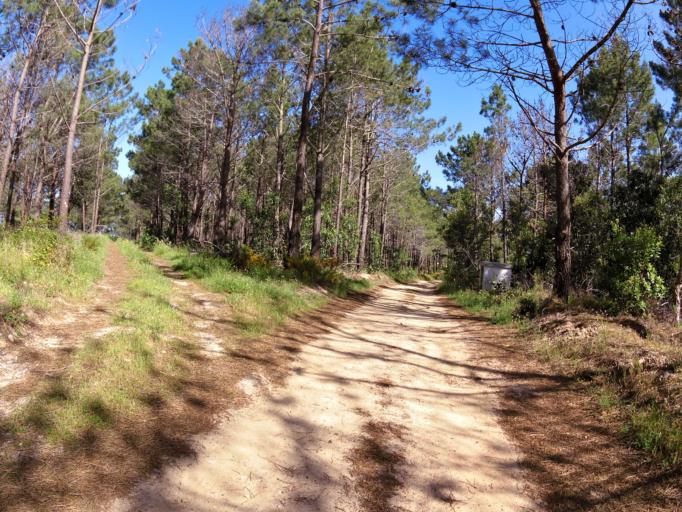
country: PT
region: Faro
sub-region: Aljezur
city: Aljezur
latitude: 37.3321
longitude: -8.8079
